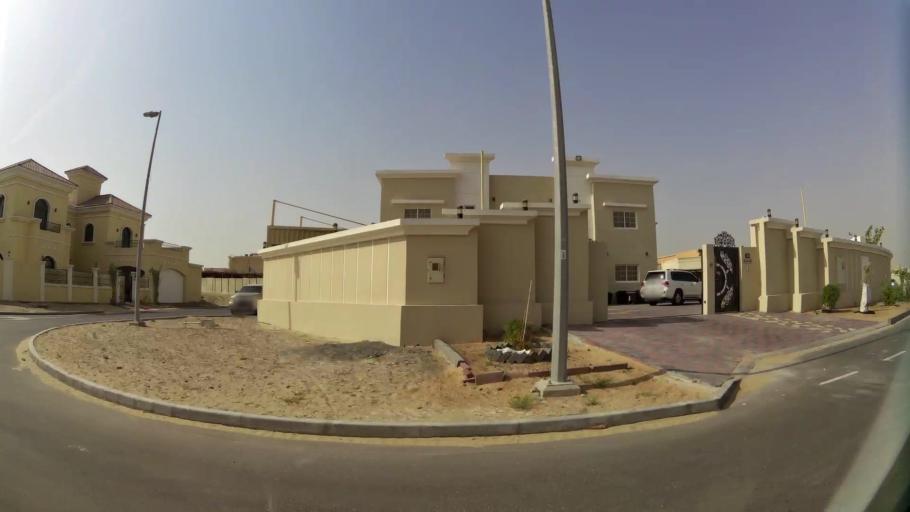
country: AE
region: Ash Shariqah
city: Sharjah
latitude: 25.2574
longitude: 55.4614
